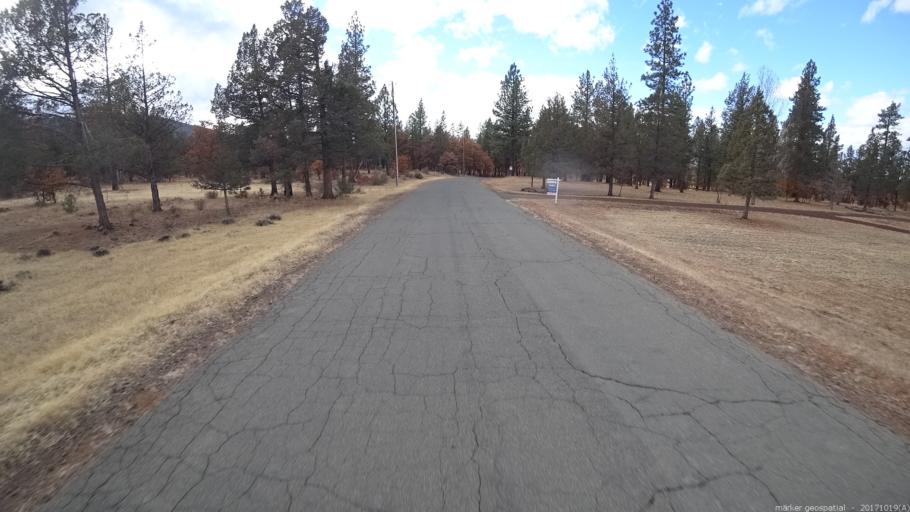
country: US
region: California
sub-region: Shasta County
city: Burney
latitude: 40.9737
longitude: -121.4400
